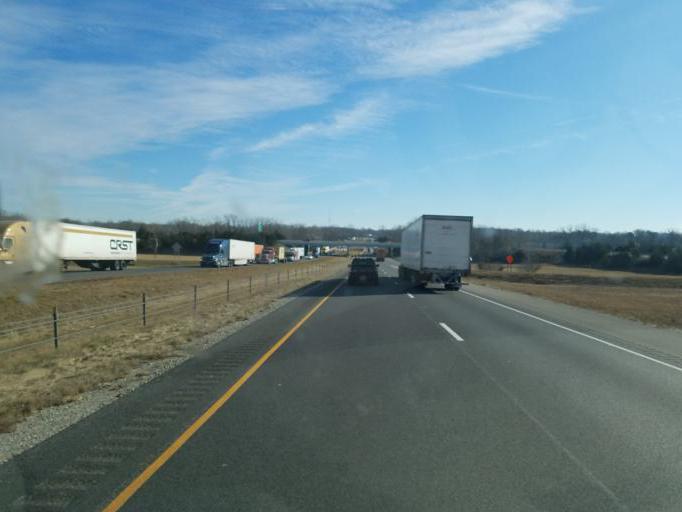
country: US
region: Indiana
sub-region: Wayne County
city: Richmond
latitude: 39.8687
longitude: -84.8631
